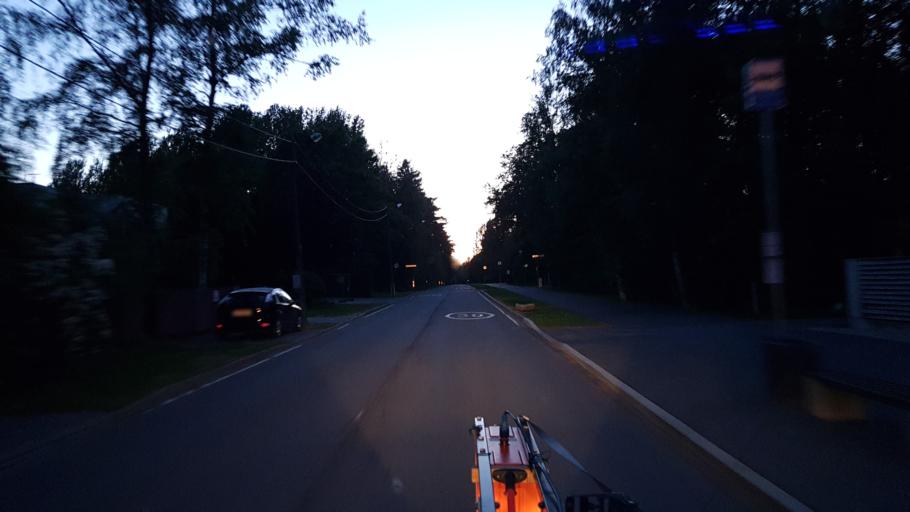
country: EE
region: Harju
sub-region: Harku vald
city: Tabasalu
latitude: 59.4559
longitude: 24.5776
